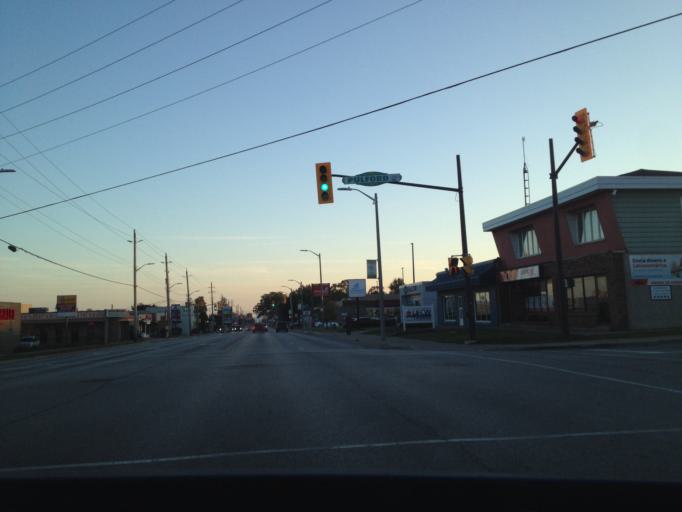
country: CA
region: Ontario
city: Amherstburg
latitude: 42.0394
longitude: -82.6007
